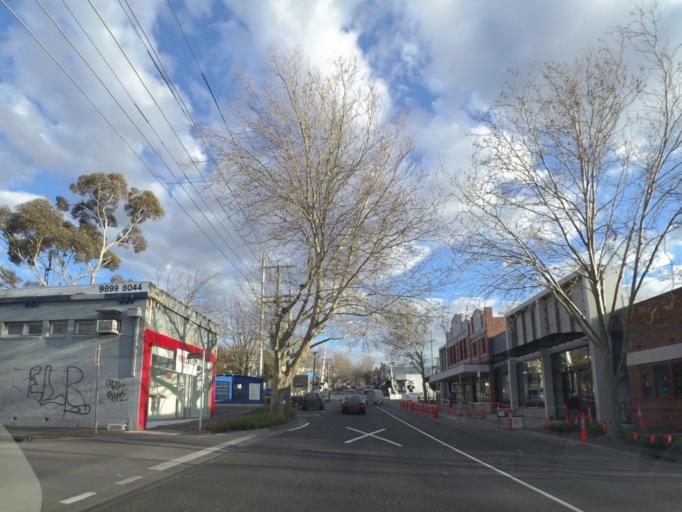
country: AU
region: Victoria
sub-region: Whitehorse
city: Surrey Hills
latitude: -37.8238
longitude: 145.0977
